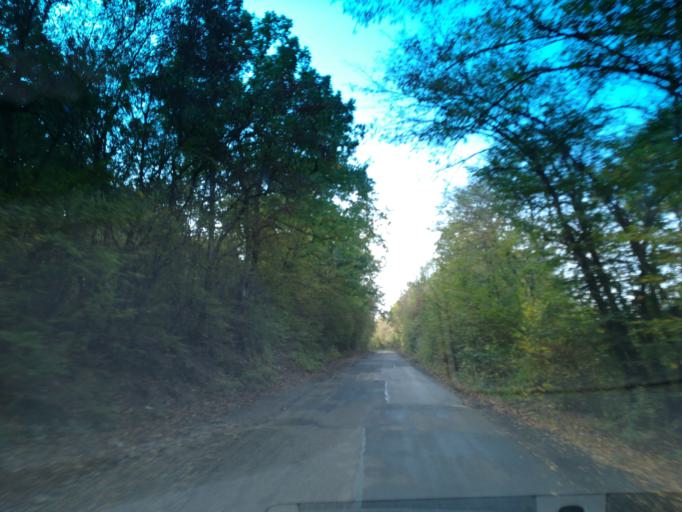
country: BG
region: Stara Zagora
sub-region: Obshtina Nikolaevo
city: Elkhovo
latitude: 42.3270
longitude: 25.3998
